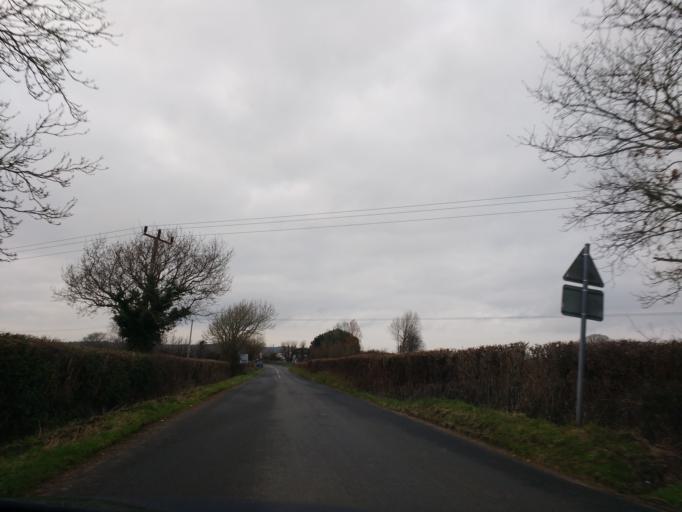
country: GB
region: England
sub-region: Isle of Wight
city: Shalfleet
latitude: 50.6978
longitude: -1.4067
